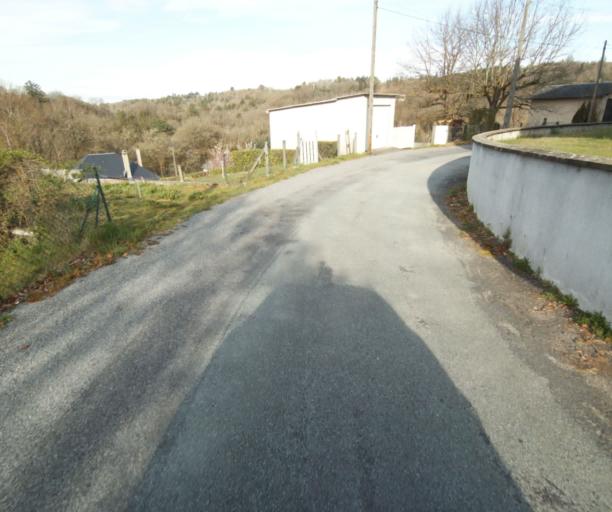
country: FR
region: Limousin
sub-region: Departement de la Correze
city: Correze
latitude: 45.3634
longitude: 1.8743
